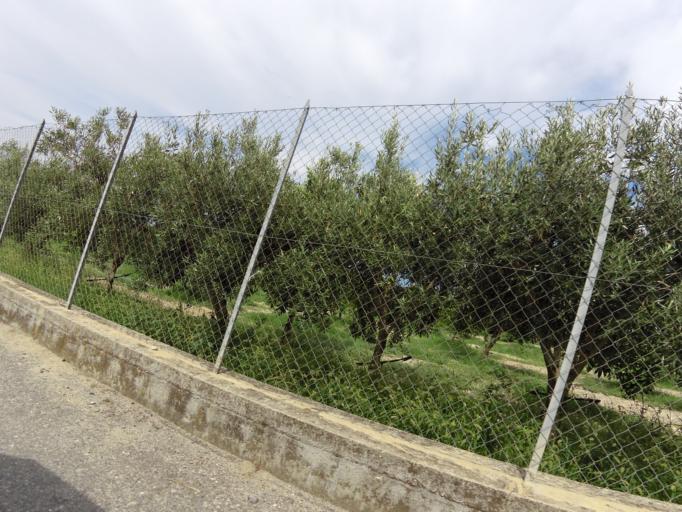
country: IT
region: Calabria
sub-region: Provincia di Reggio Calabria
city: Monasterace
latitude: 38.4581
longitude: 16.5136
